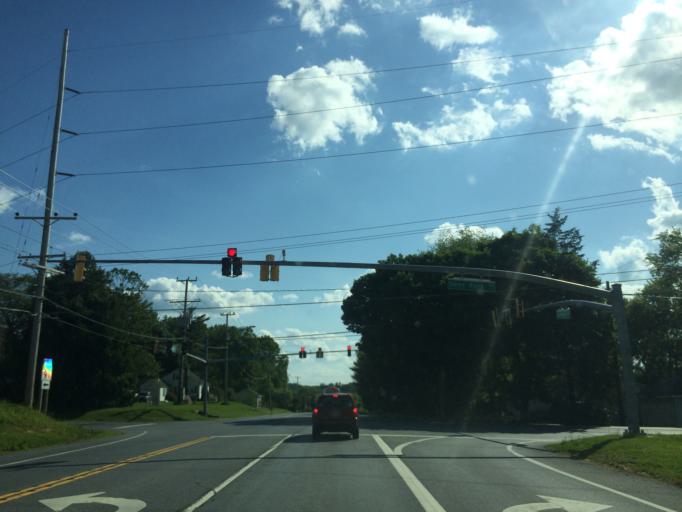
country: US
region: Maryland
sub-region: Carroll County
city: Eldersburg
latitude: 39.4776
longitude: -76.9133
